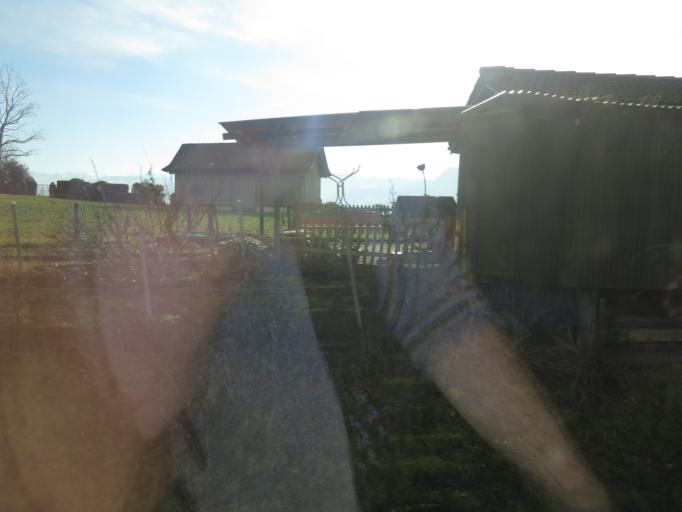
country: CH
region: Zurich
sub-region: Bezirk Meilen
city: Uerikon
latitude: 47.2355
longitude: 8.7680
